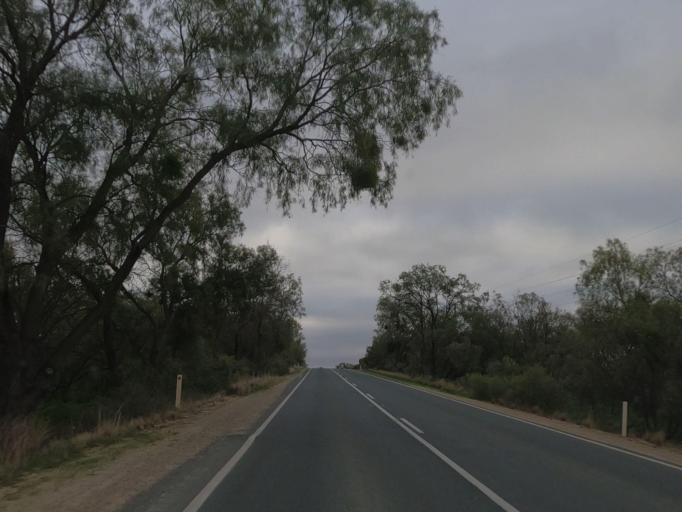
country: AU
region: Victoria
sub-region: Swan Hill
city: Swan Hill
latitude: -35.4688
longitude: 143.6608
